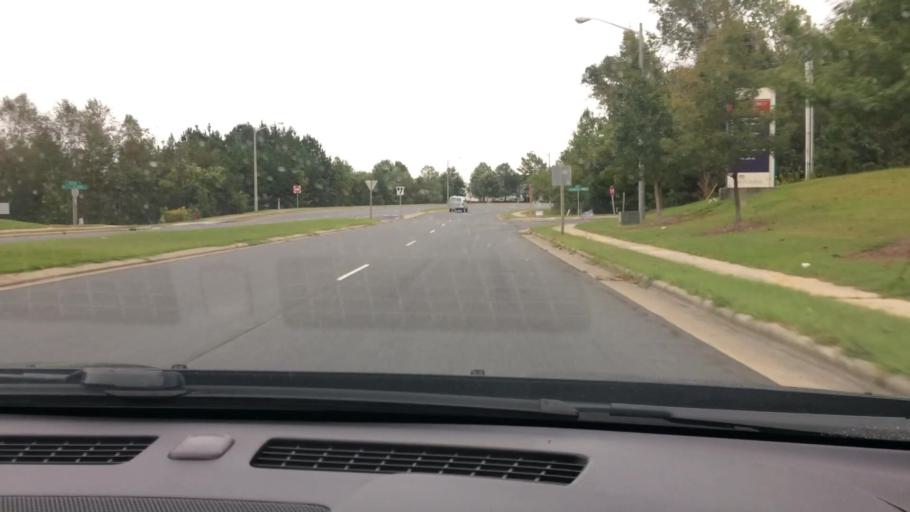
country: US
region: North Carolina
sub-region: Pitt County
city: Greenville
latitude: 35.6121
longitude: -77.4106
